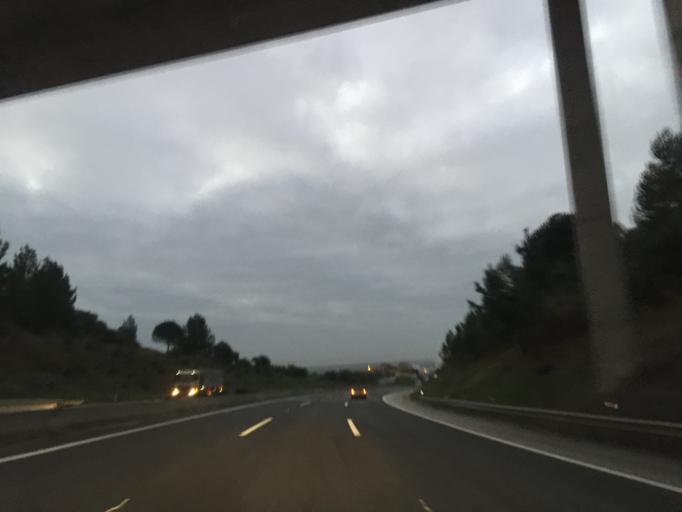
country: PT
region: Lisbon
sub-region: Vila Franca de Xira
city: Sobralinho
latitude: 38.9035
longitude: -9.0573
